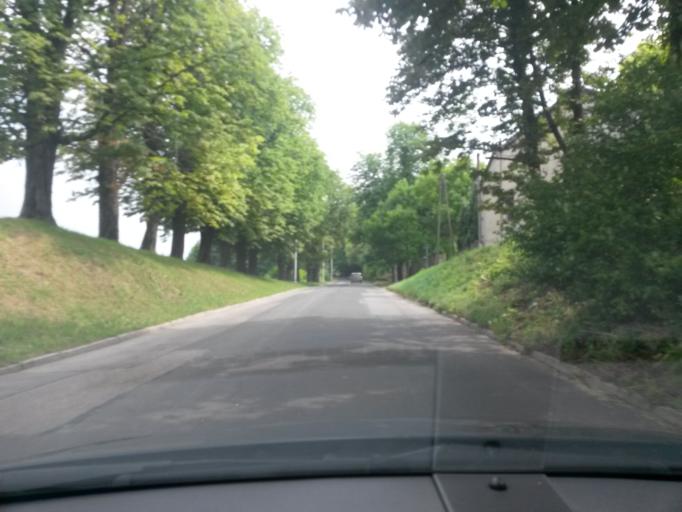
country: PL
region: Silesian Voivodeship
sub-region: Powiat czestochowski
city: Huta Stara B
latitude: 50.7637
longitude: 19.1543
